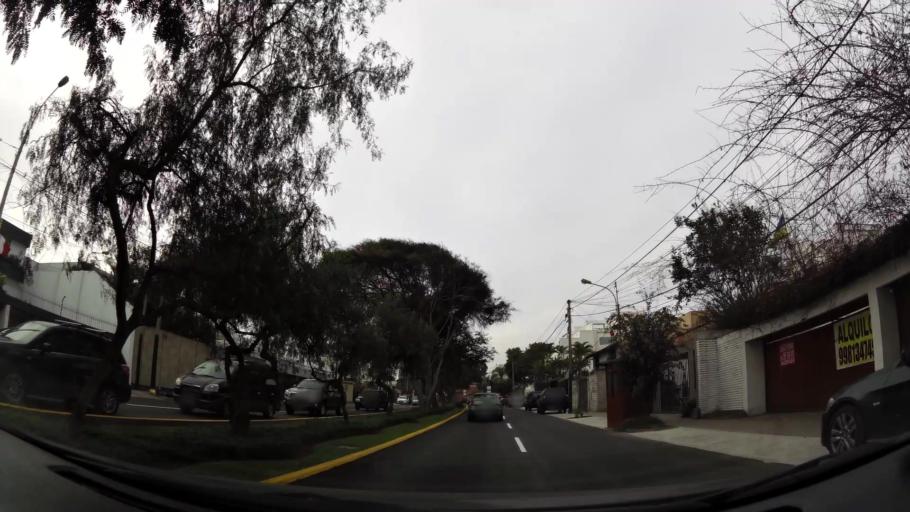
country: PE
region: Lima
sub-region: Lima
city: San Isidro
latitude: -12.1075
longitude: -77.0535
